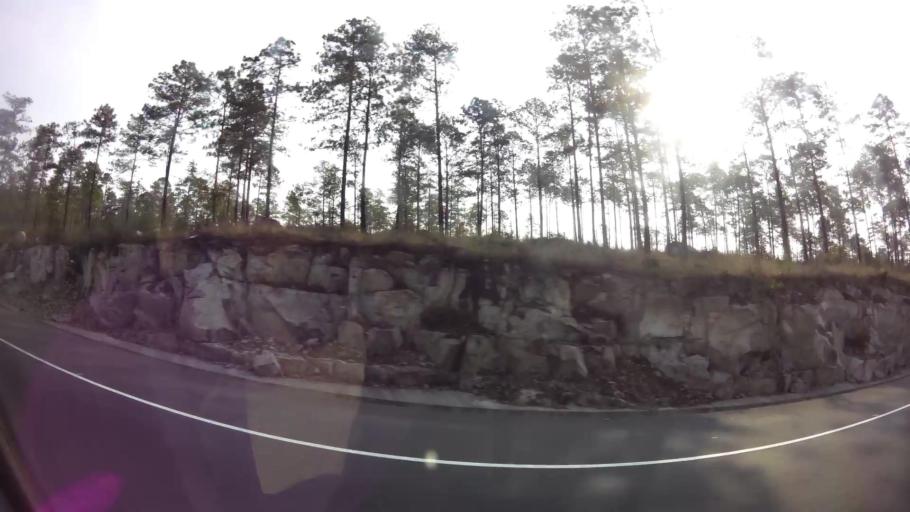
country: HN
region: Francisco Morazan
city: Zambrano
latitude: 14.2883
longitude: -87.4086
